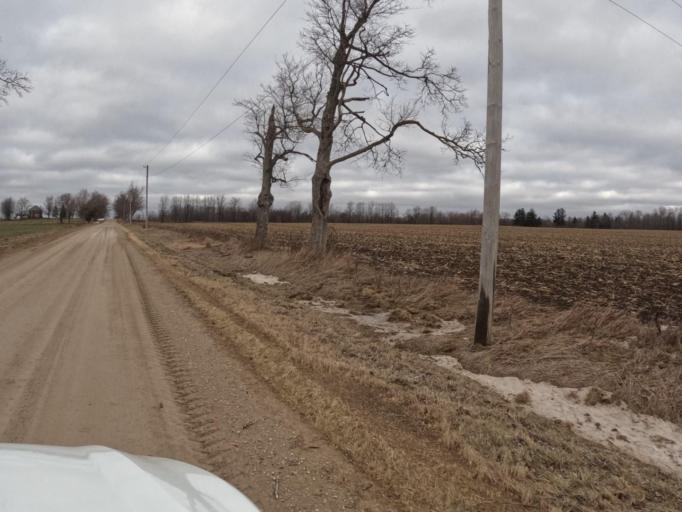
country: CA
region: Ontario
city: Shelburne
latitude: 43.8839
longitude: -80.4050
